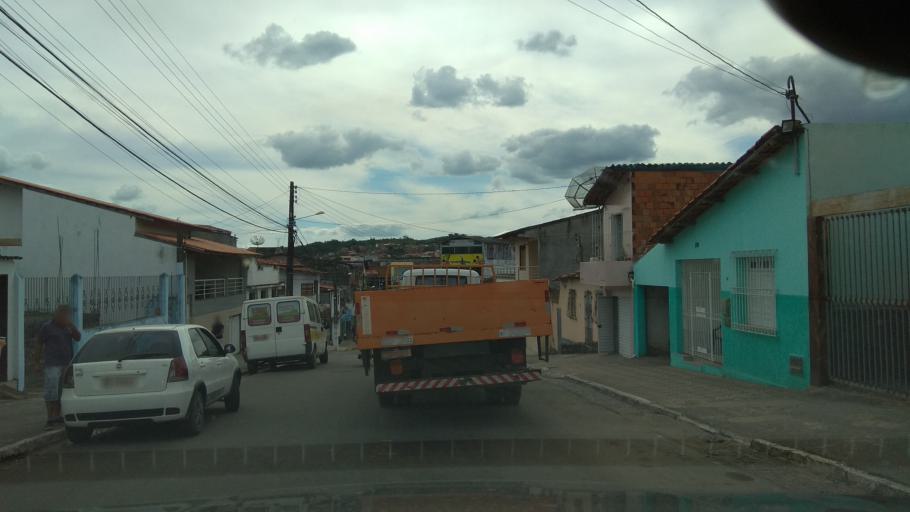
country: BR
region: Bahia
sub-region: Ipiau
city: Ipiau
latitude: -14.1358
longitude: -39.7376
